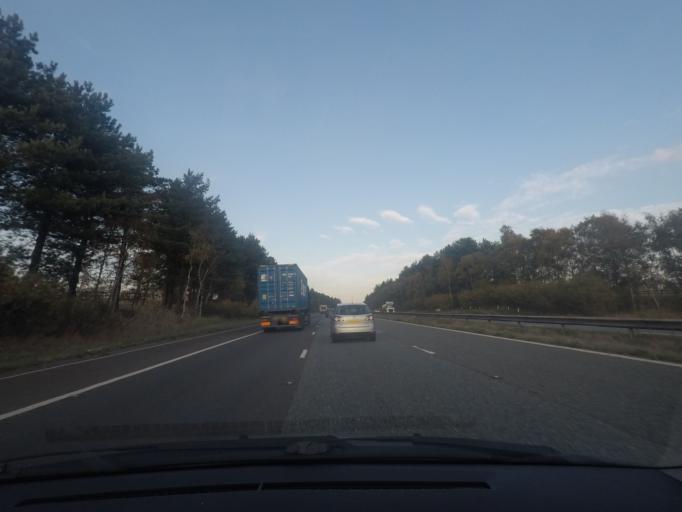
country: GB
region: England
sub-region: North Lincolnshire
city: Worlaby
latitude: 53.5720
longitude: -0.4708
